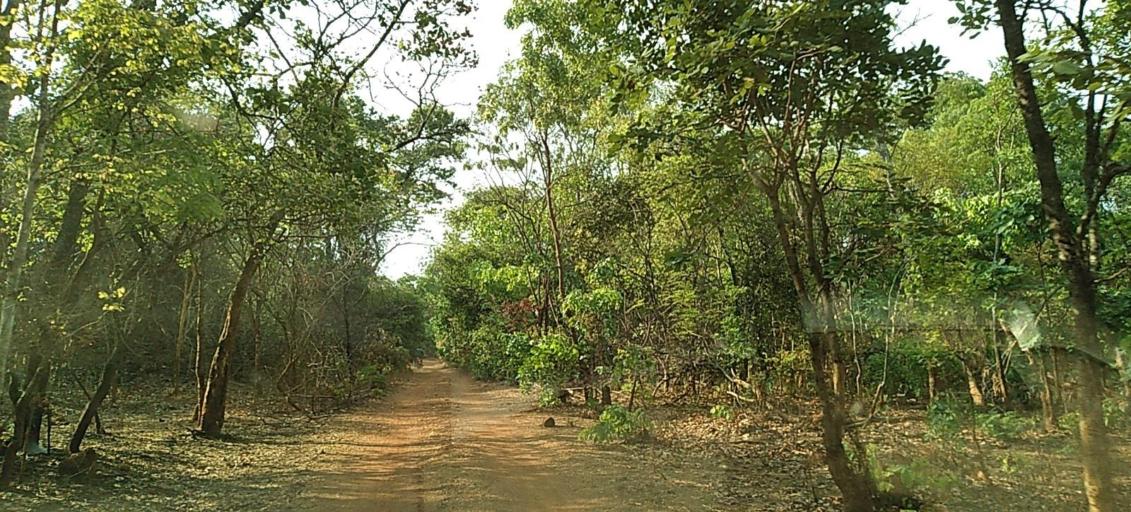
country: ZM
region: Copperbelt
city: Kalulushi
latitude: -12.9661
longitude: 27.7128
